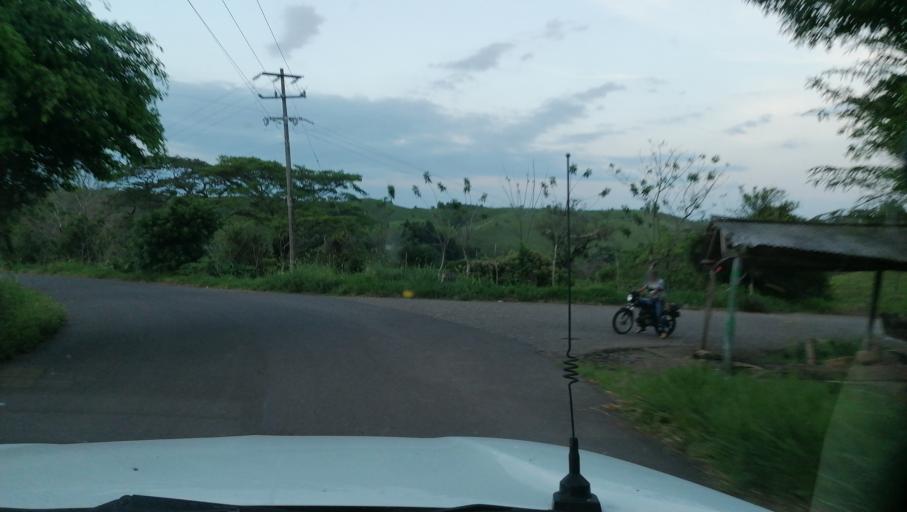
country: MX
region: Chiapas
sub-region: Ostuacan
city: Nuevo Juan del Grijalva
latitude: 17.4385
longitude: -93.3502
